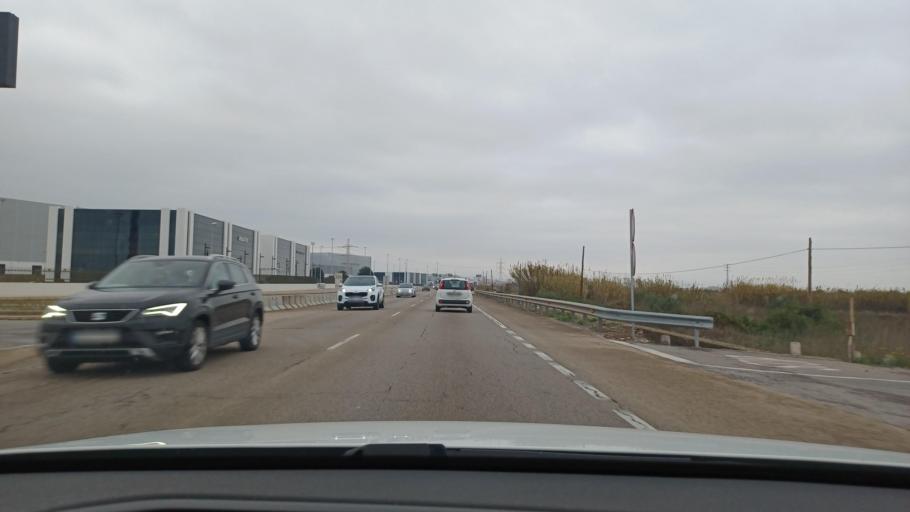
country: ES
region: Valencia
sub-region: Provincia de Castello
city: Alquerias del Nino Perdido
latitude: 39.9115
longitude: -0.1137
